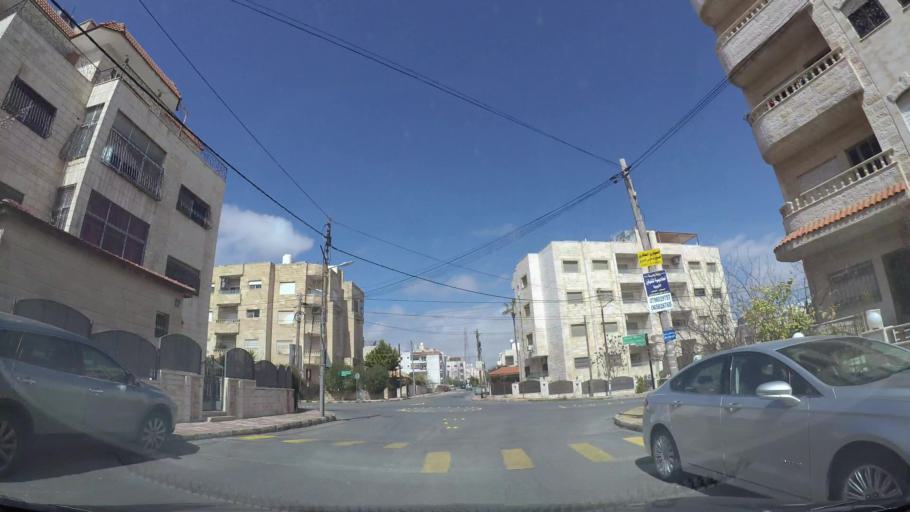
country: JO
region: Amman
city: Wadi as Sir
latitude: 31.9596
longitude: 35.8427
